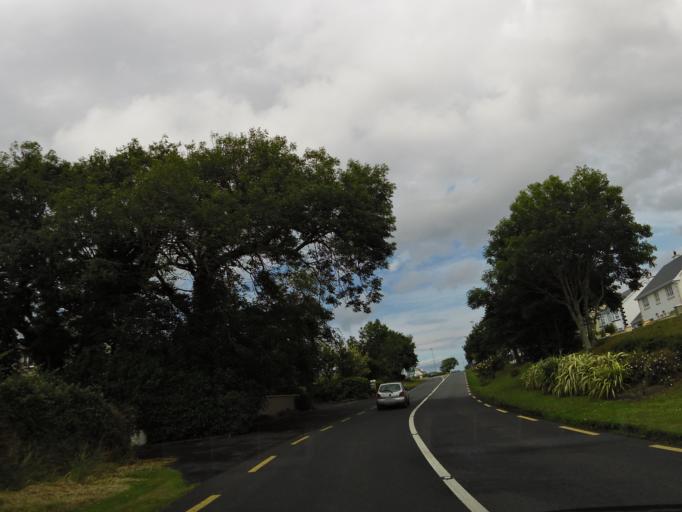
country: IE
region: Munster
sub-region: An Clar
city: Kilrush
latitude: 52.6430
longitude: -9.4929
